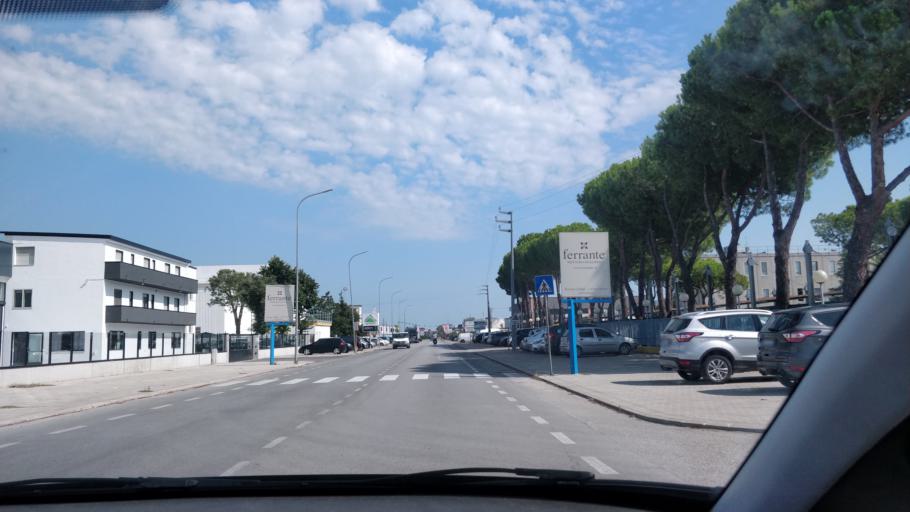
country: IT
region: Abruzzo
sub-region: Provincia di Pescara
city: Santa Teresa
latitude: 42.4113
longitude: 14.1672
